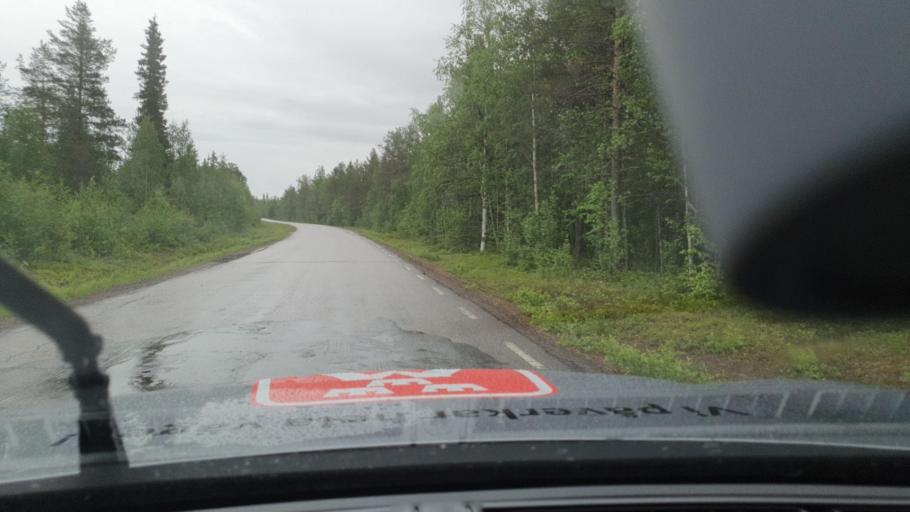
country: SE
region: Norrbotten
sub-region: Pajala Kommun
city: Pajala
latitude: 66.8421
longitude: 23.0749
